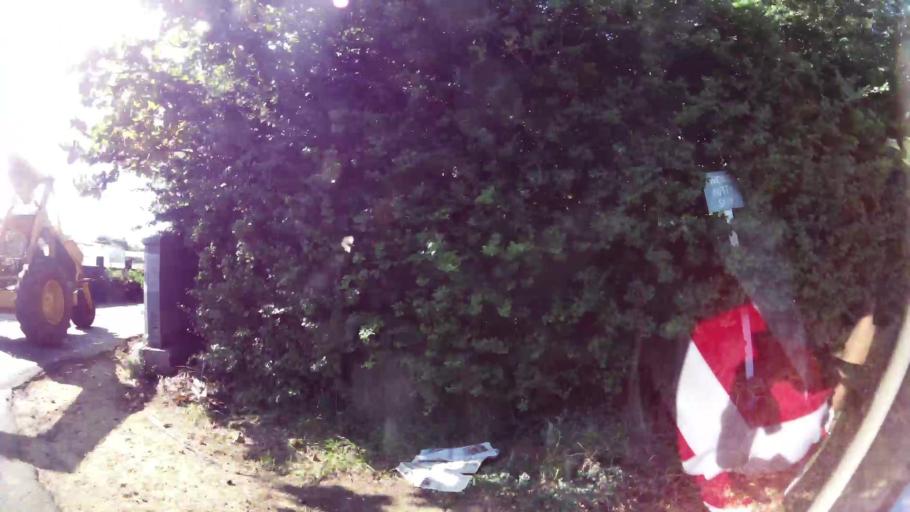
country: MU
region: Black River
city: Albion
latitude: -20.2076
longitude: 57.4062
